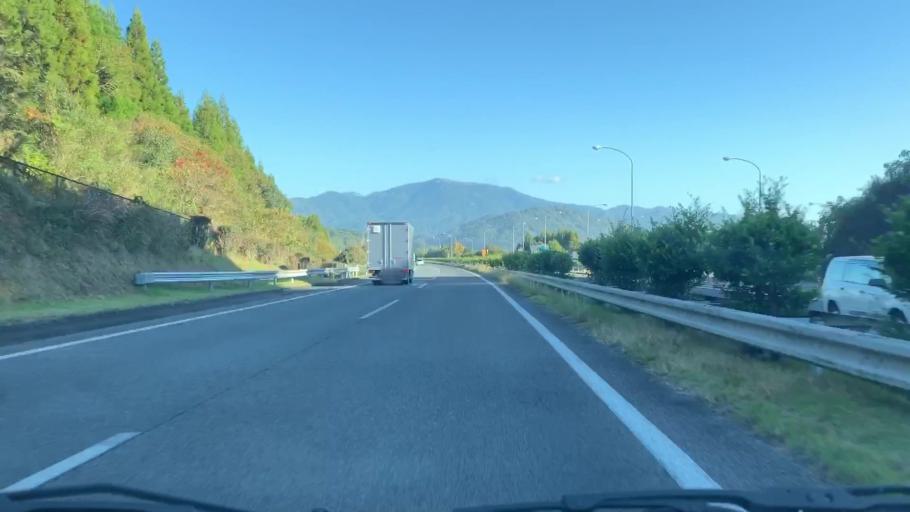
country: JP
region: Saga Prefecture
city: Takeocho-takeo
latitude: 33.2515
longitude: 130.0772
